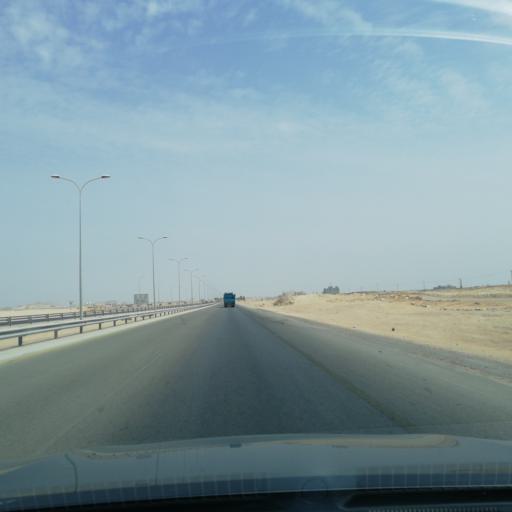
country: OM
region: Zufar
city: Salalah
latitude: 17.5958
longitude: 54.0384
